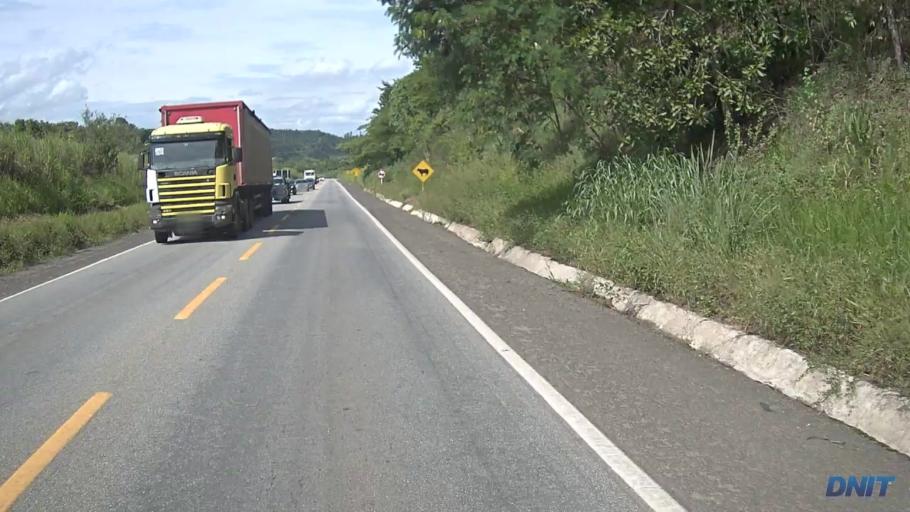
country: BR
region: Minas Gerais
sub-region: Ipaba
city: Ipaba
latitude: -19.3920
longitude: -42.4807
